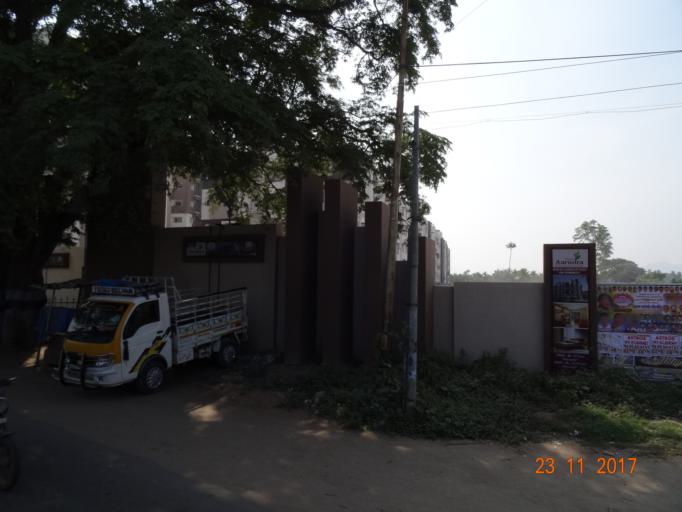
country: IN
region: Tamil Nadu
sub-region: Coimbatore
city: Perur
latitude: 10.9840
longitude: 76.9261
